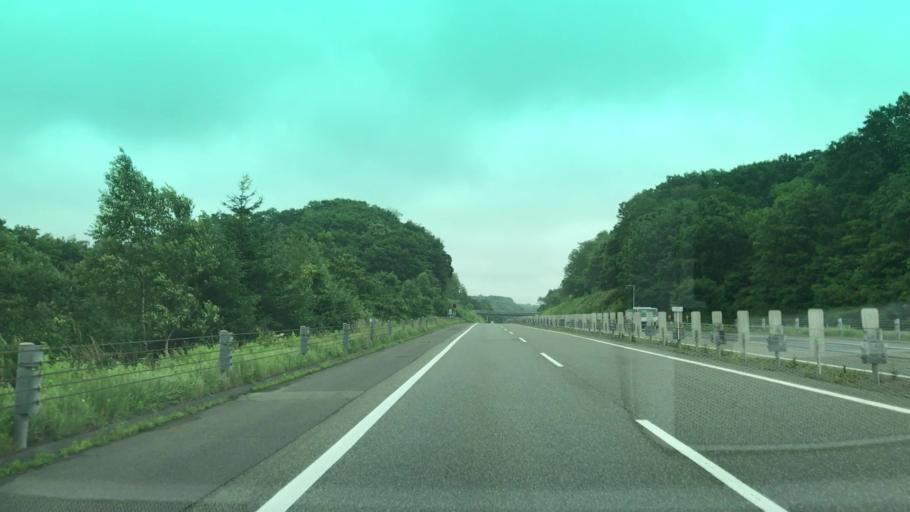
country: JP
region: Hokkaido
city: Tomakomai
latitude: 42.6452
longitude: 141.5295
